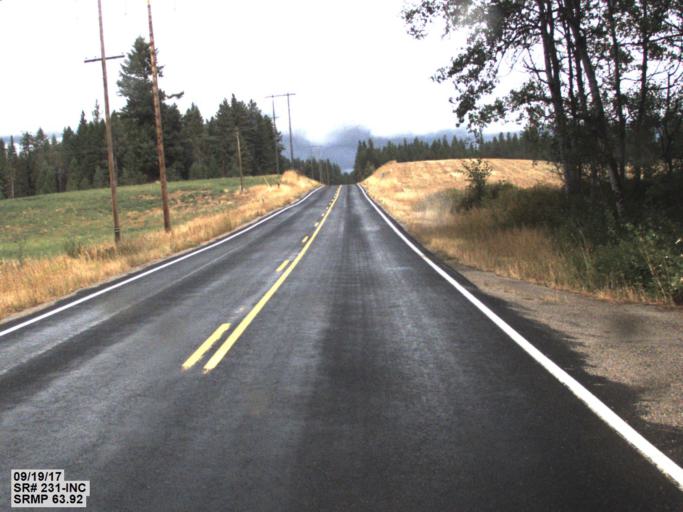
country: US
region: Washington
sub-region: Stevens County
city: Chewelah
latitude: 48.0704
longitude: -117.7624
